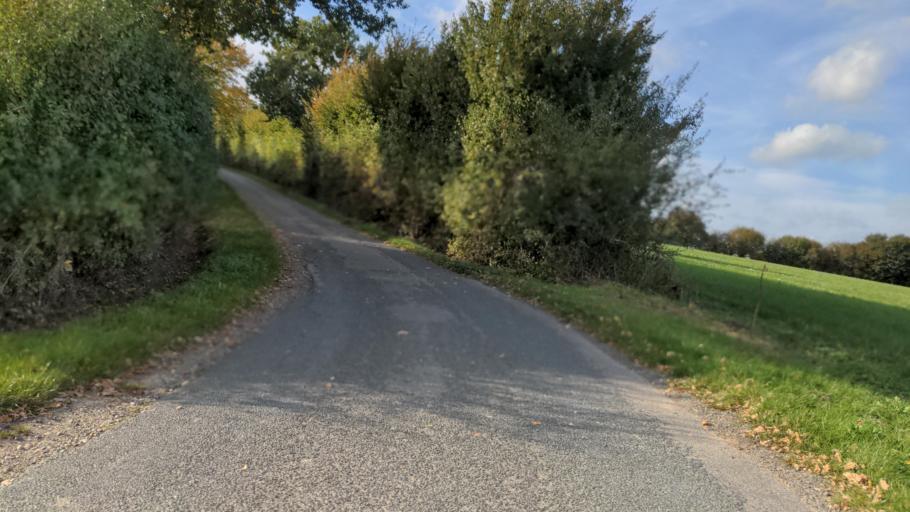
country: DE
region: Schleswig-Holstein
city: Monkhagen
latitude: 53.9411
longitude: 10.5701
